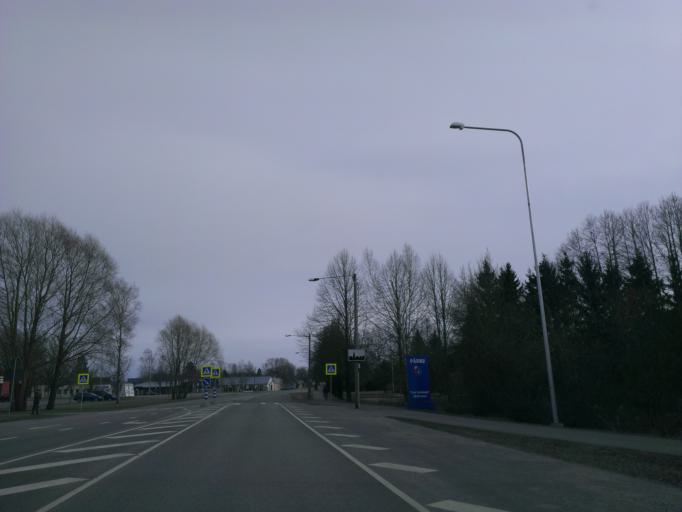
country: EE
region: Paernumaa
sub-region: Paernu linn
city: Parnu
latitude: 58.3941
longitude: 24.4592
